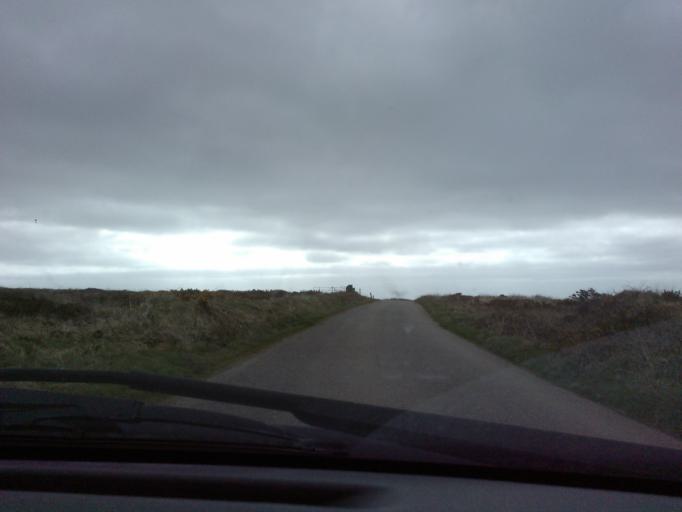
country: GB
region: England
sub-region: Cornwall
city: St. Buryan
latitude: 50.1567
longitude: -5.6207
